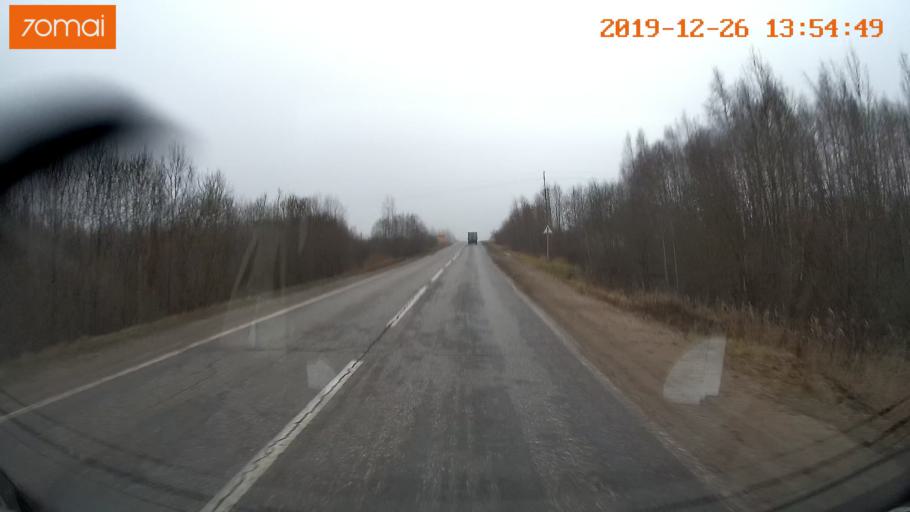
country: RU
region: Jaroslavl
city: Poshekhon'ye
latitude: 58.6098
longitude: 38.6398
